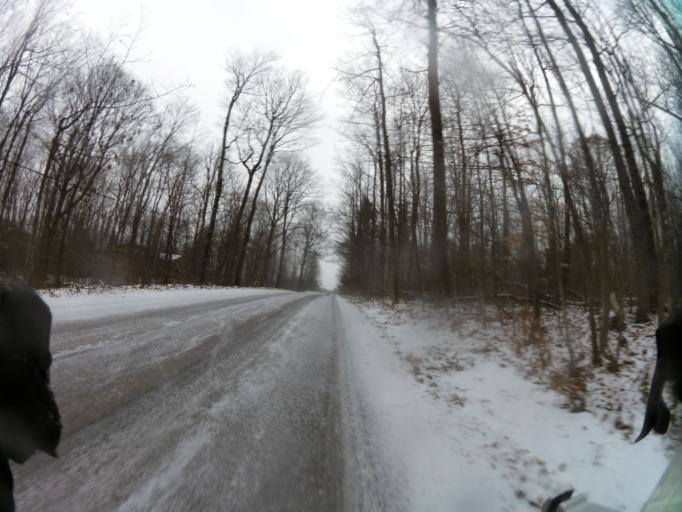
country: CA
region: Quebec
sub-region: Outaouais
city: Gatineau
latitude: 45.4871
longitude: -75.8405
